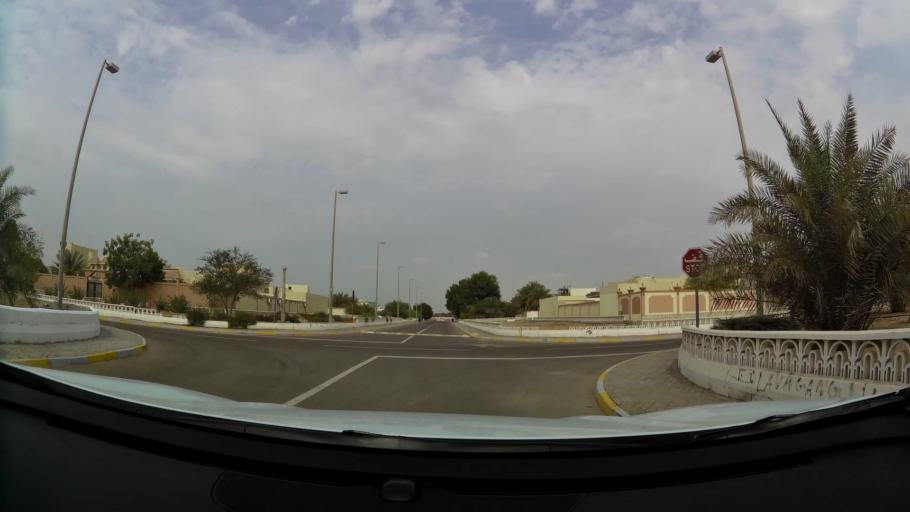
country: AE
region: Abu Dhabi
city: Abu Dhabi
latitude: 24.6465
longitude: 54.7295
